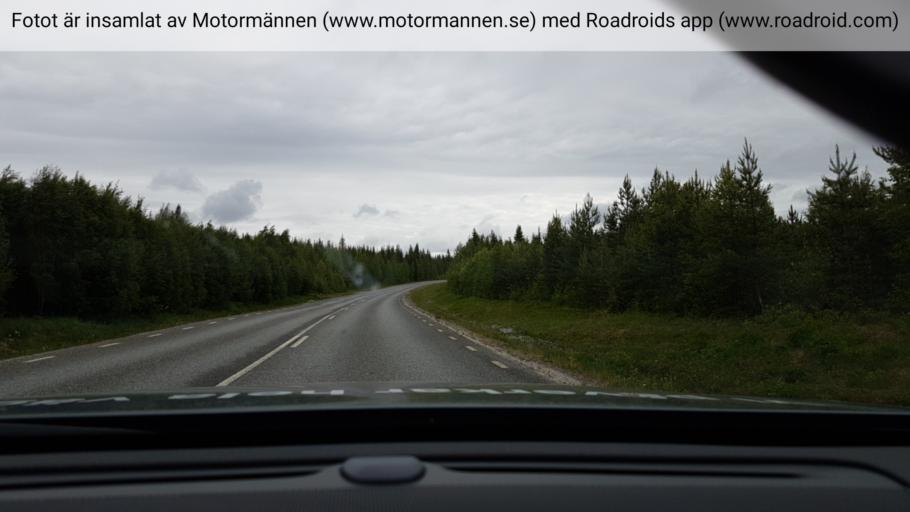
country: SE
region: Vaesterbotten
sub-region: Lycksele Kommun
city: Lycksele
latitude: 64.5283
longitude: 18.4505
